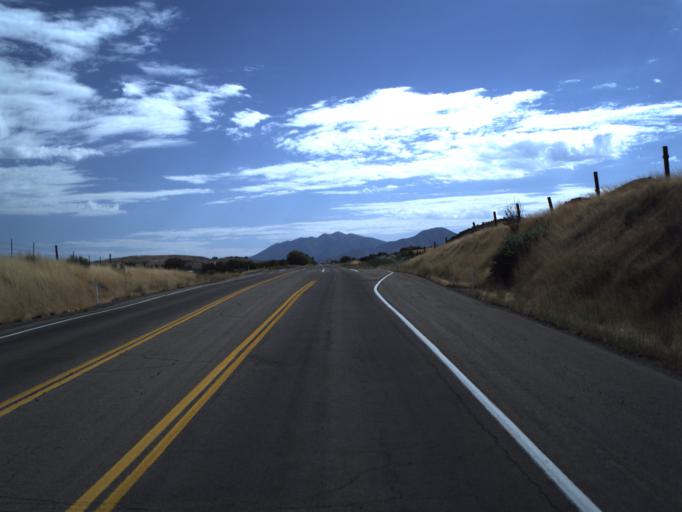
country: US
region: Utah
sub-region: Utah County
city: Genola
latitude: 39.9759
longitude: -111.8454
